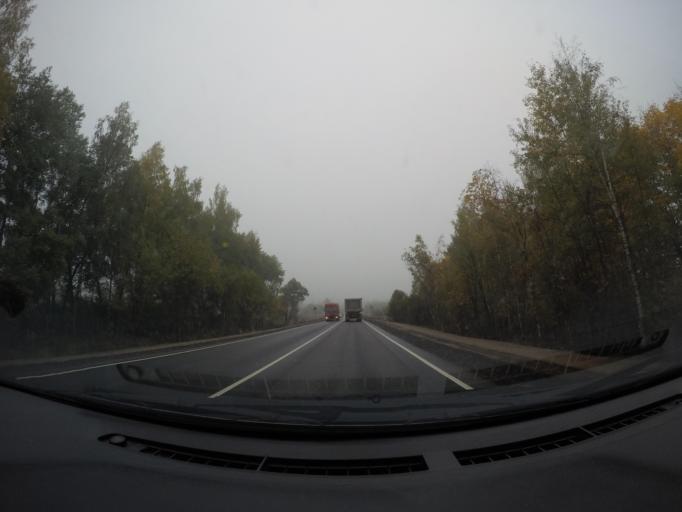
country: RU
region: Moskovskaya
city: Rumyantsevo
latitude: 55.8663
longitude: 36.5367
